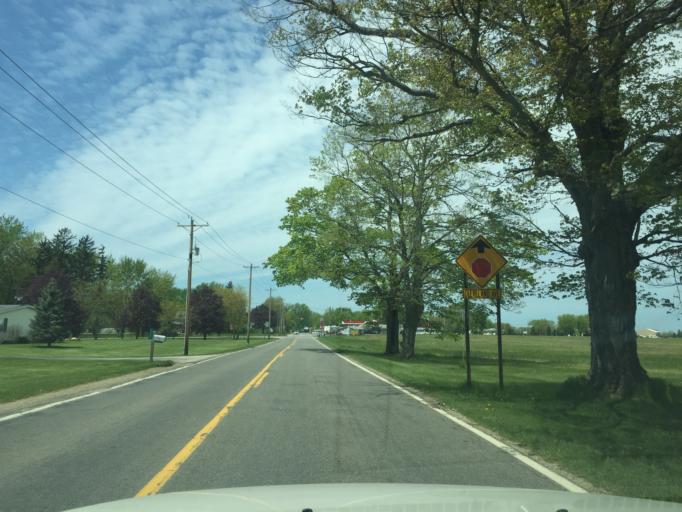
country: US
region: Michigan
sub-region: Berrien County
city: Stevensville
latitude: 41.9754
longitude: -86.4934
